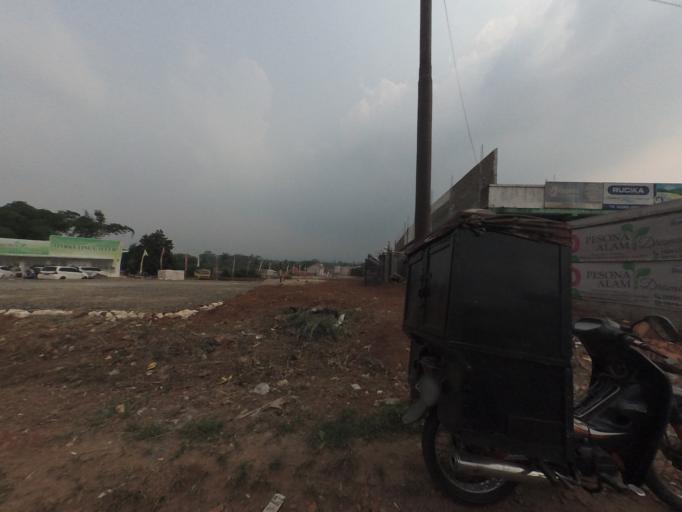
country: ID
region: West Java
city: Ciampea
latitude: -6.5632
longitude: 106.6823
